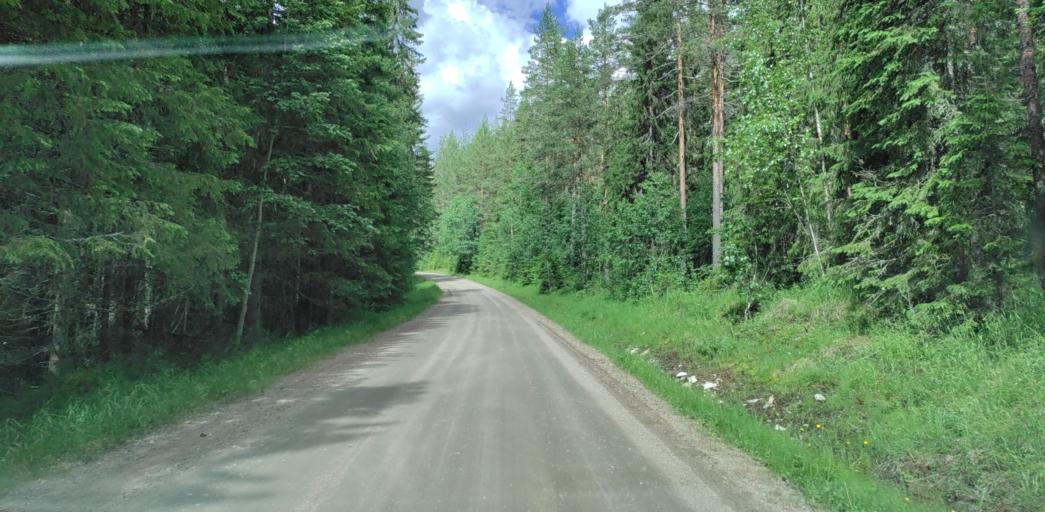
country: SE
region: Vaermland
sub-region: Hagfors Kommun
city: Ekshaerad
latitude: 60.0991
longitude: 13.3923
